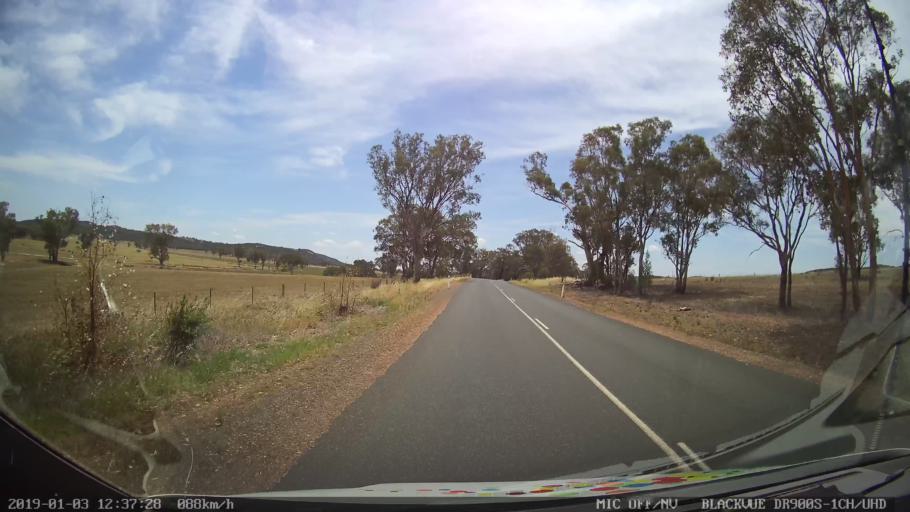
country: AU
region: New South Wales
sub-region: Weddin
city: Grenfell
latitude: -33.8422
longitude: 148.1847
